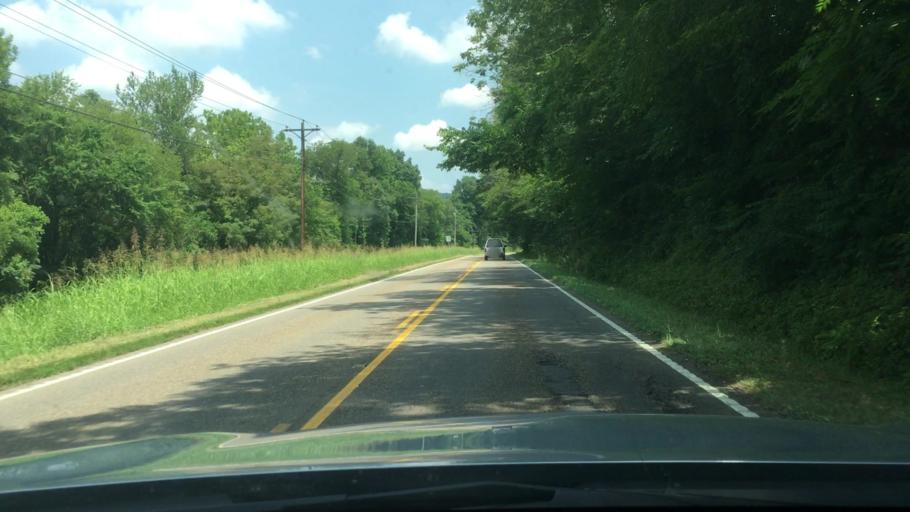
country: US
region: Tennessee
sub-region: Cocke County
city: Newport
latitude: 35.9534
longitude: -83.1286
